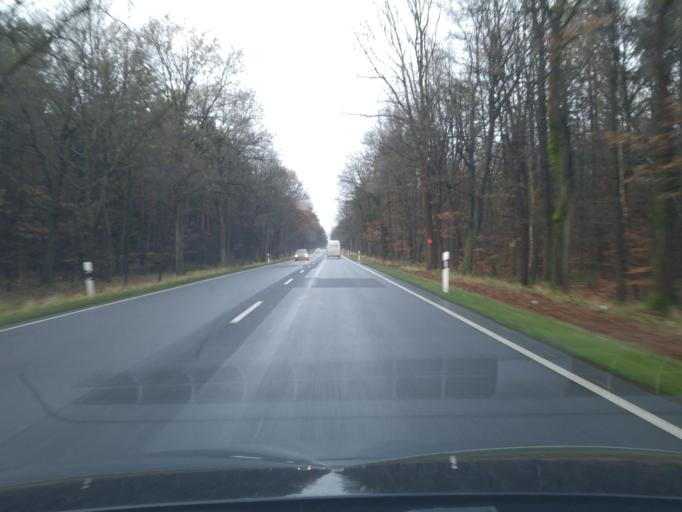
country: DE
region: Lower Saxony
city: Dedelstorf
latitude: 52.7135
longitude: 10.4801
